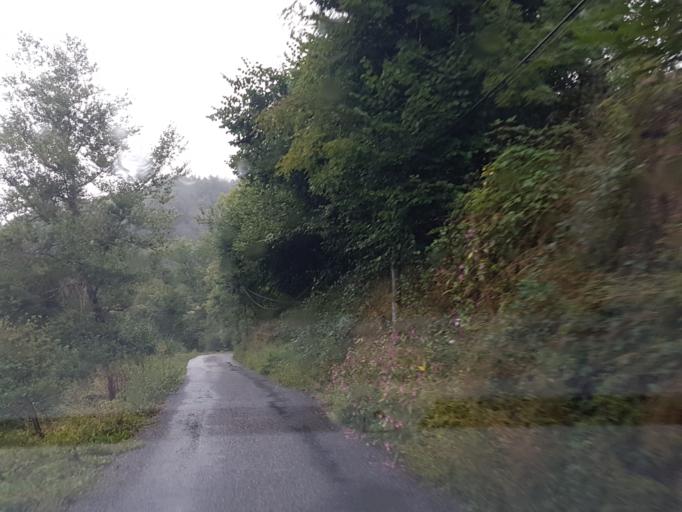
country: FR
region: Midi-Pyrenees
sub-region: Departement de l'Ariege
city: Montjoie-en-Couserans
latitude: 42.9025
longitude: 1.3548
